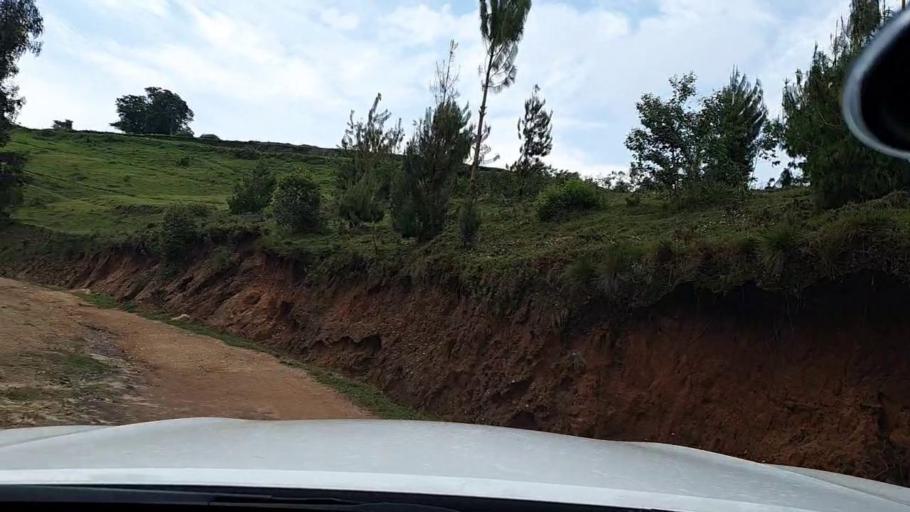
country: RW
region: Western Province
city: Kibuye
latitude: -2.2019
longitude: 29.3210
